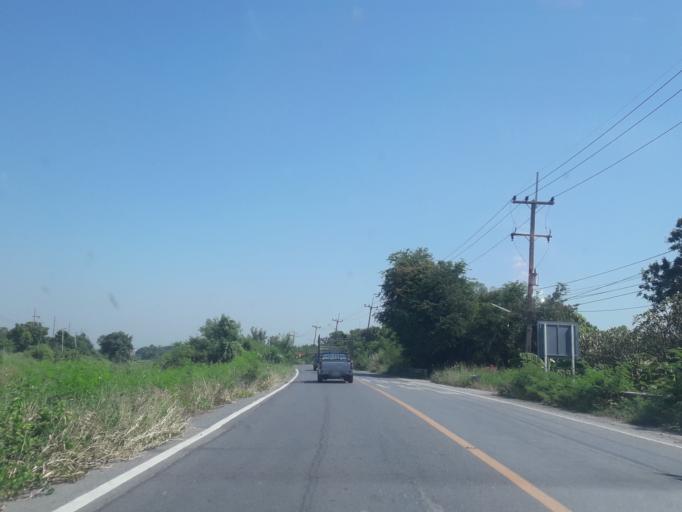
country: TH
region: Sara Buri
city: Nong Khae
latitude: 14.3198
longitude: 100.8672
